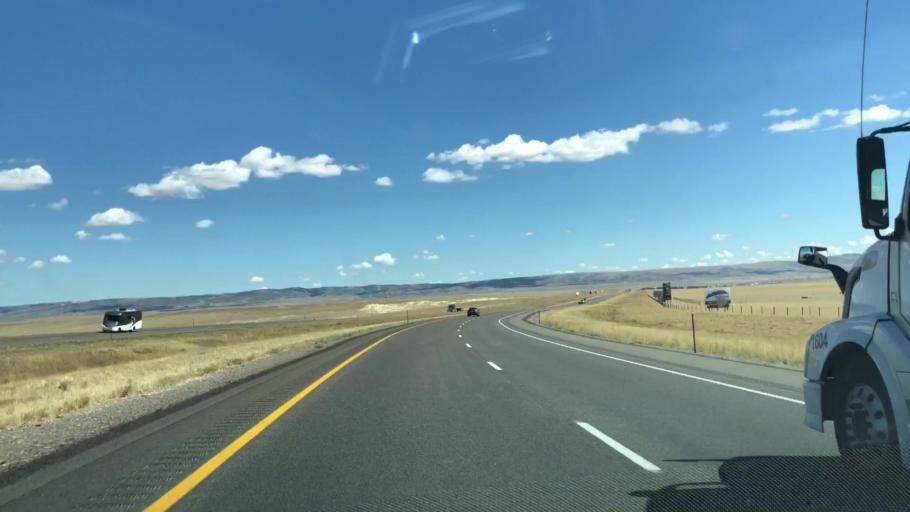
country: US
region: Wyoming
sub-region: Albany County
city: Laramie
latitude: 41.3496
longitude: -105.6992
